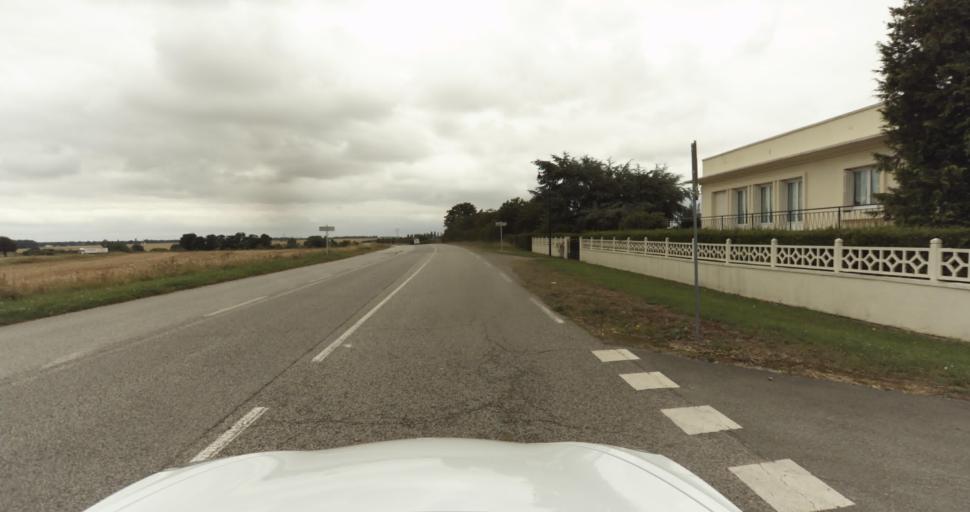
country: FR
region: Haute-Normandie
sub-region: Departement de l'Eure
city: Saint-Sebastien-de-Morsent
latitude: 49.0347
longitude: 1.0955
